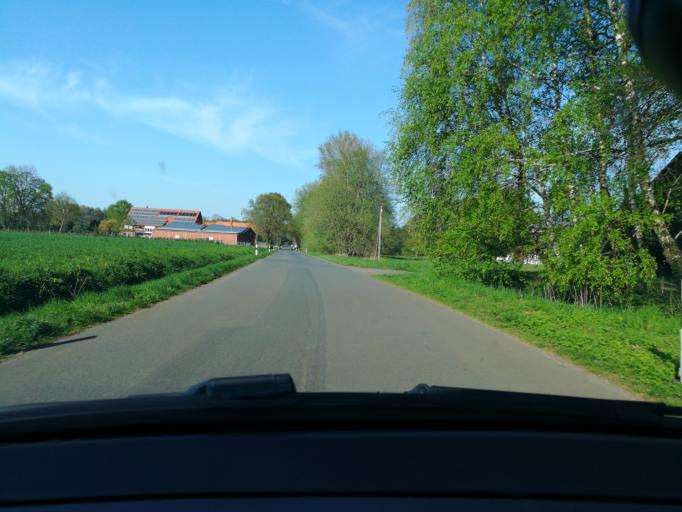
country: DE
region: North Rhine-Westphalia
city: Versmold
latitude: 52.0085
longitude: 8.1223
